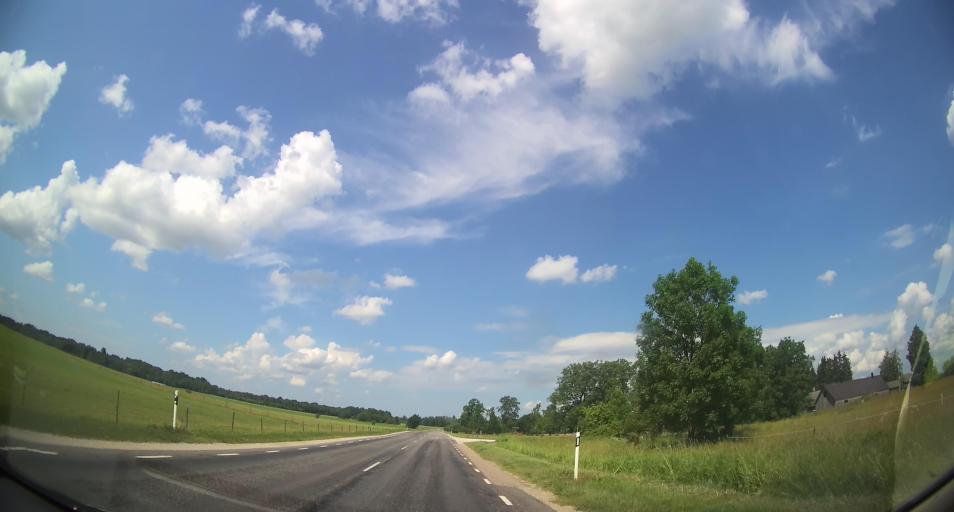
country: EE
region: Harju
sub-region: Nissi vald
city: Turba
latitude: 58.9004
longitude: 24.2228
